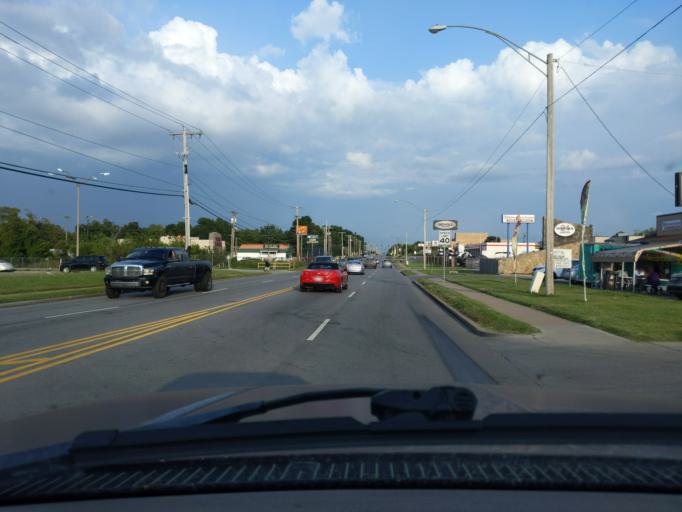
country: US
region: Oklahoma
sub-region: Tulsa County
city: Tulsa
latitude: 36.1334
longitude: -95.9032
